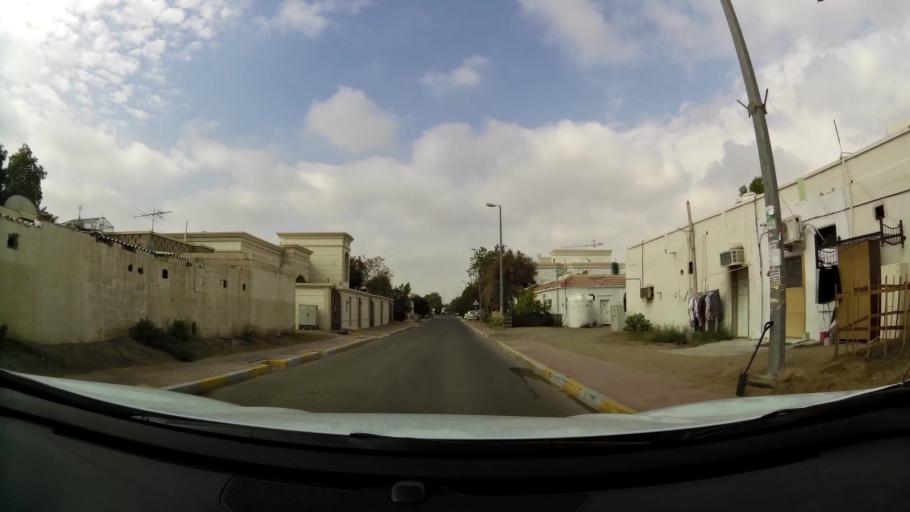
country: AE
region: Abu Dhabi
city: Al Ain
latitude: 24.2253
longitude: 55.7548
